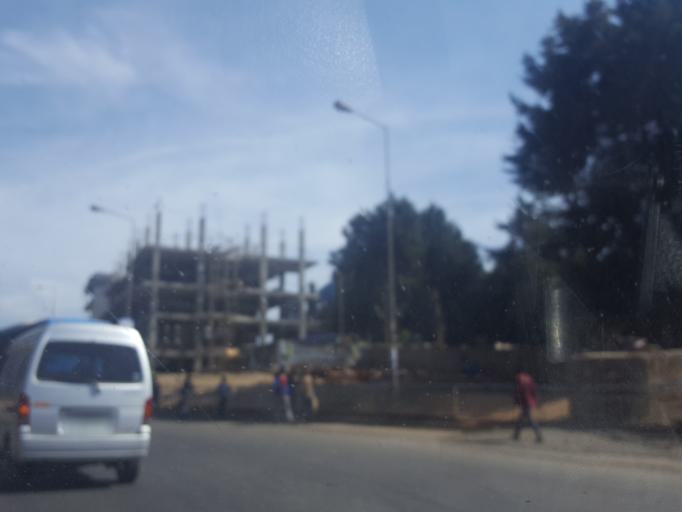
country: ET
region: Adis Abeba
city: Addis Ababa
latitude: 9.0567
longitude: 38.7135
